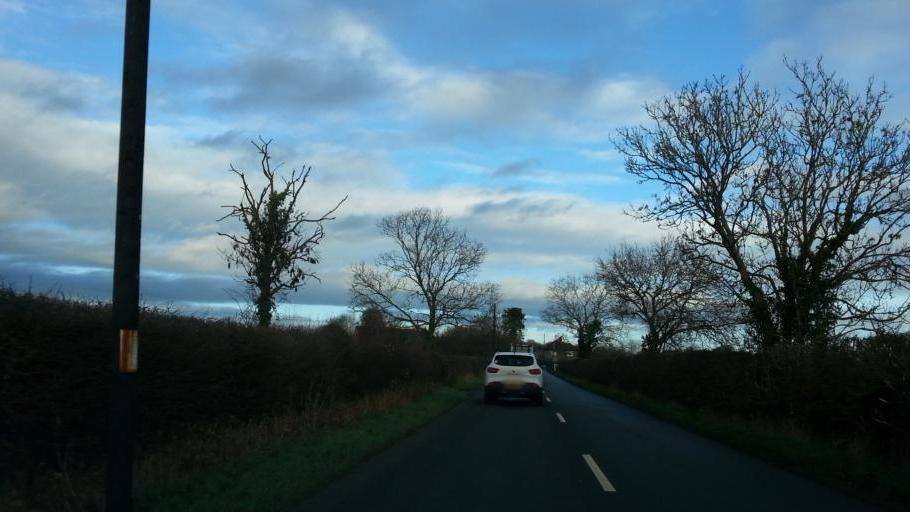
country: GB
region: England
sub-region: Oxfordshire
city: Faringdon
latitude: 51.6367
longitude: -1.5498
